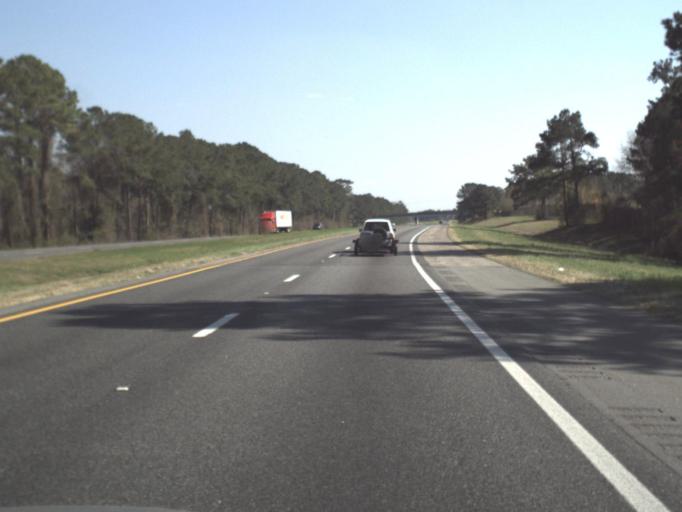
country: US
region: Florida
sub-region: Gadsden County
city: Gretna
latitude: 30.6000
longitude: -84.7279
